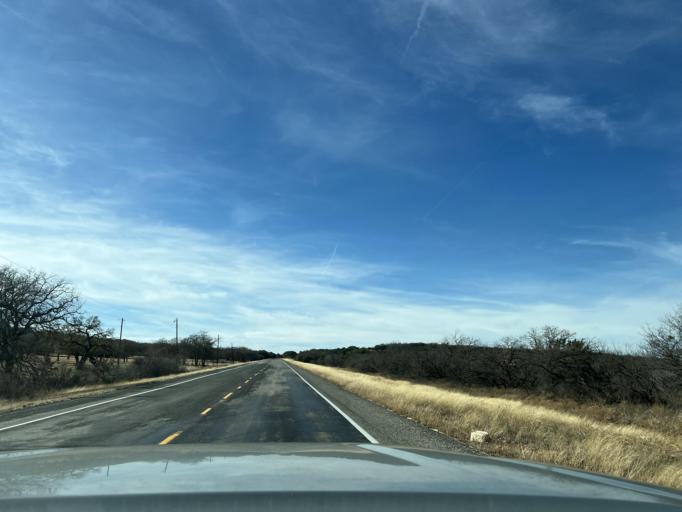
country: US
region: Texas
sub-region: Eastland County
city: Cisco
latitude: 32.4646
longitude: -99.0239
